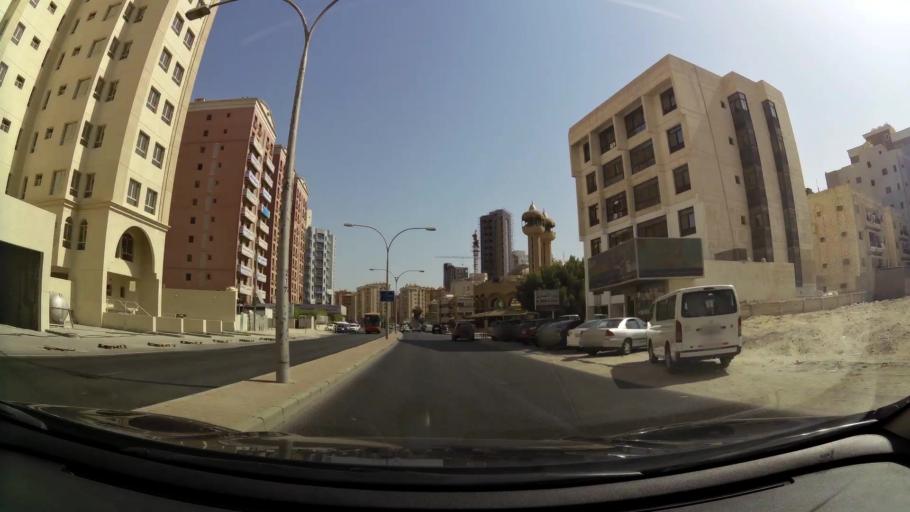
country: KW
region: Muhafazat Hawalli
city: Hawalli
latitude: 29.3368
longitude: 48.0505
